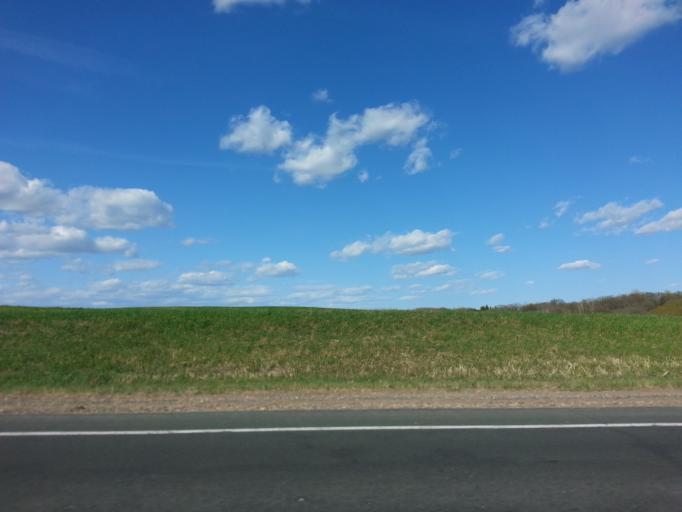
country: US
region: Wisconsin
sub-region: Saint Croix County
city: Somerset
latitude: 45.0429
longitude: -92.6877
